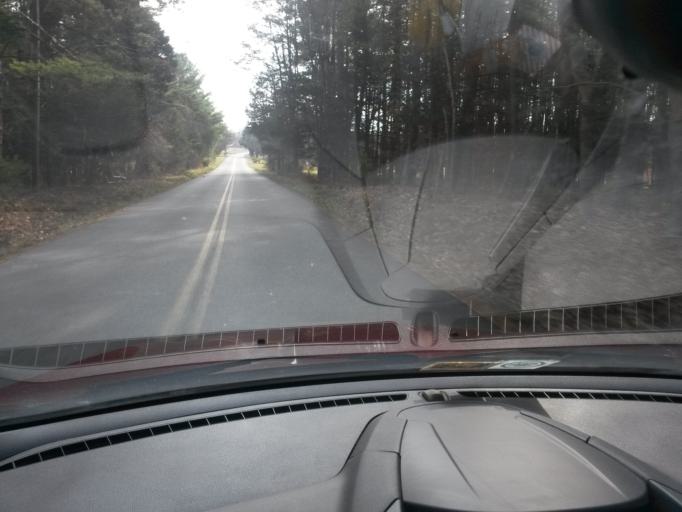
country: US
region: Virginia
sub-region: Botetourt County
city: Fincastle
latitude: 37.5480
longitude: -79.8780
